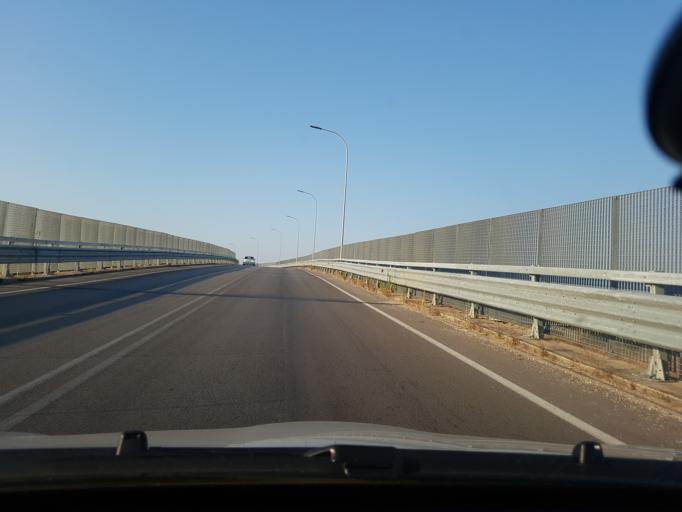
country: IT
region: Apulia
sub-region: Provincia di Foggia
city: Carapelle
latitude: 41.4051
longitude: 15.6520
